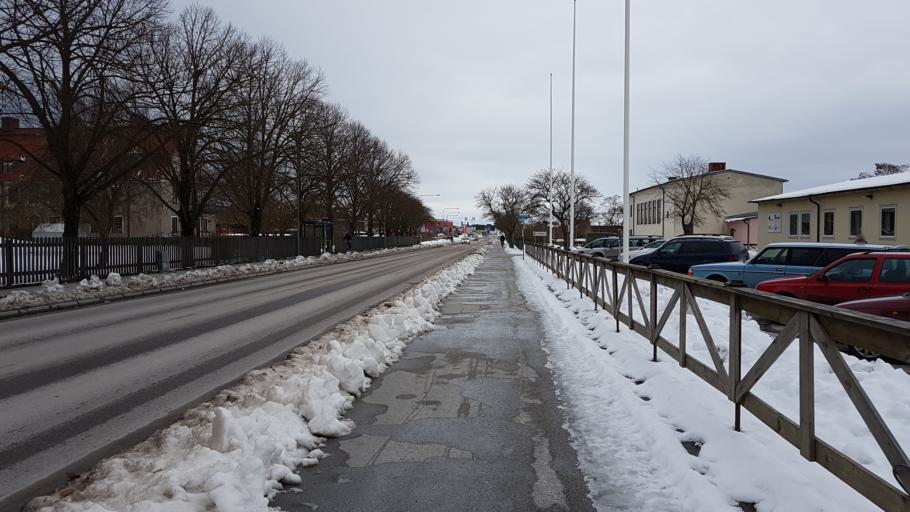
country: SE
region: Gotland
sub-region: Gotland
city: Visby
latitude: 57.6421
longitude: 18.3104
